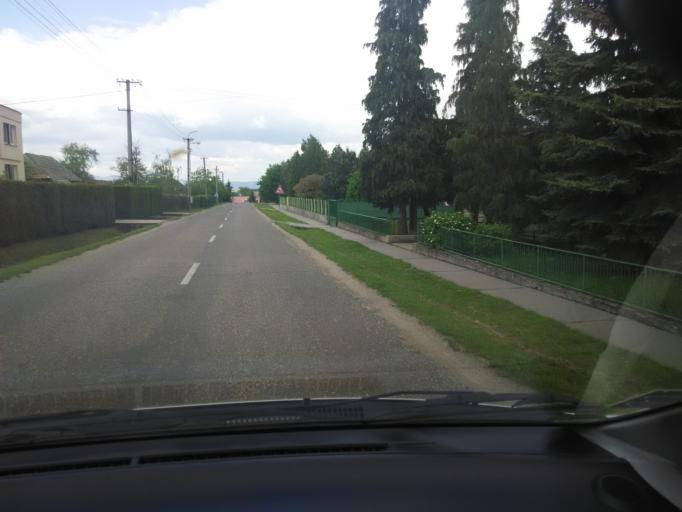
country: SK
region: Nitriansky
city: Levice
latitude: 48.1287
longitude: 18.4616
